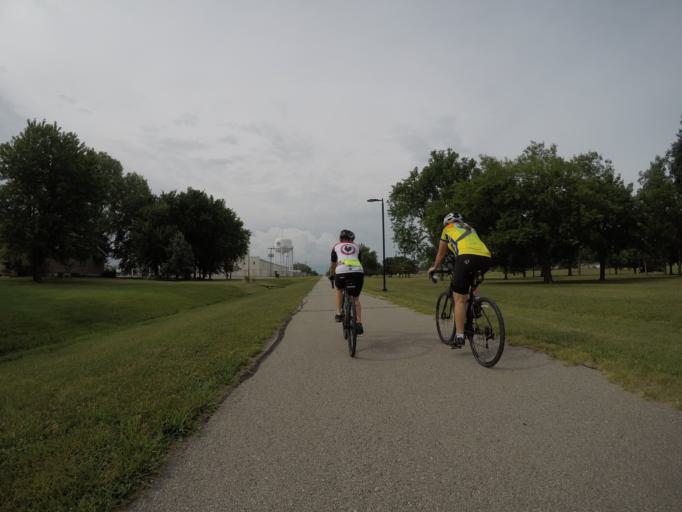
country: US
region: Kansas
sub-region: Franklin County
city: Ottawa
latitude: 38.5962
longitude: -95.2704
